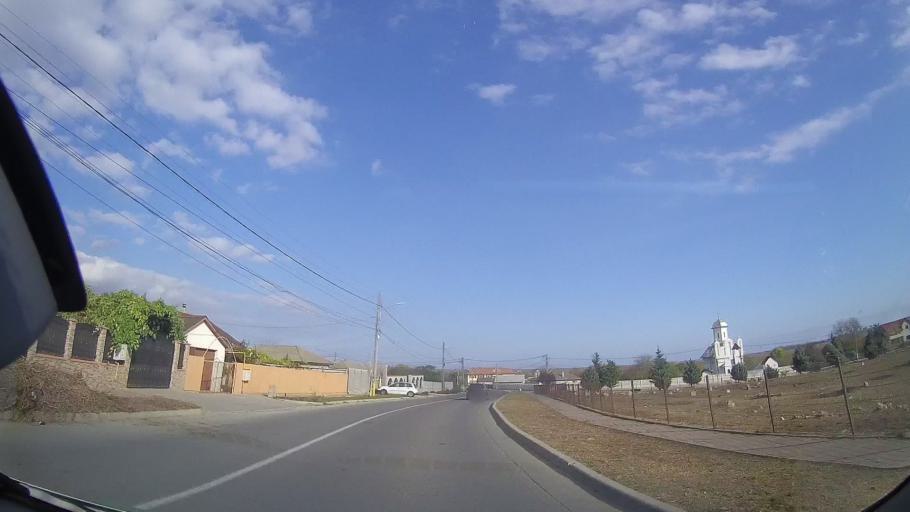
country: RO
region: Constanta
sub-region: Comuna Douazeci si Trei August
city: Dulcesti
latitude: 43.9041
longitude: 28.5429
